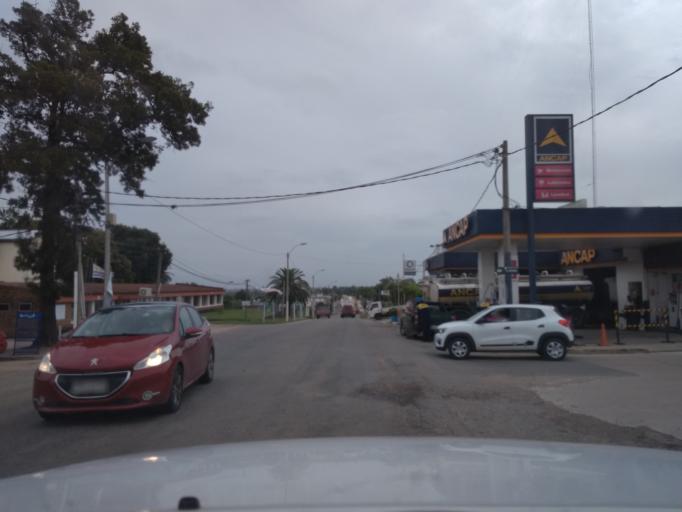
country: UY
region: Canelones
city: Tala
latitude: -34.3473
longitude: -55.7633
